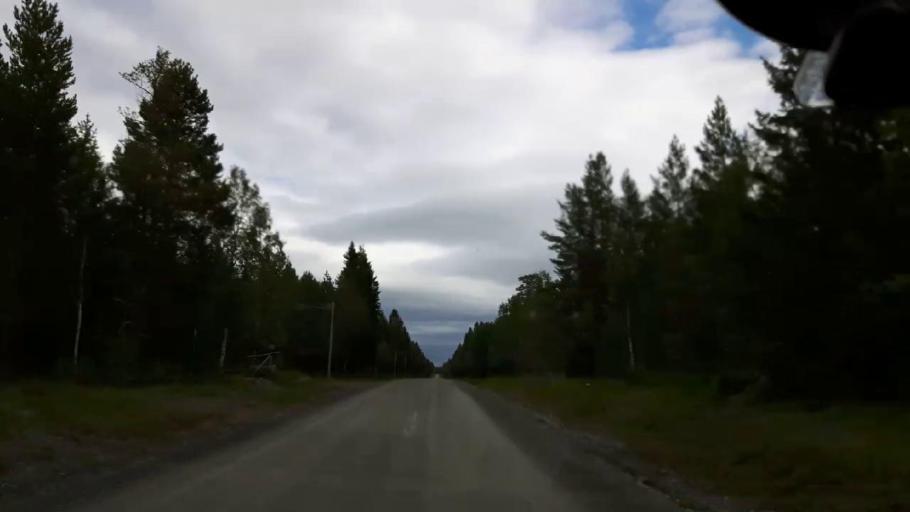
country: SE
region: Jaemtland
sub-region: OEstersunds Kommun
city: Brunflo
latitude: 63.0990
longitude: 14.9446
